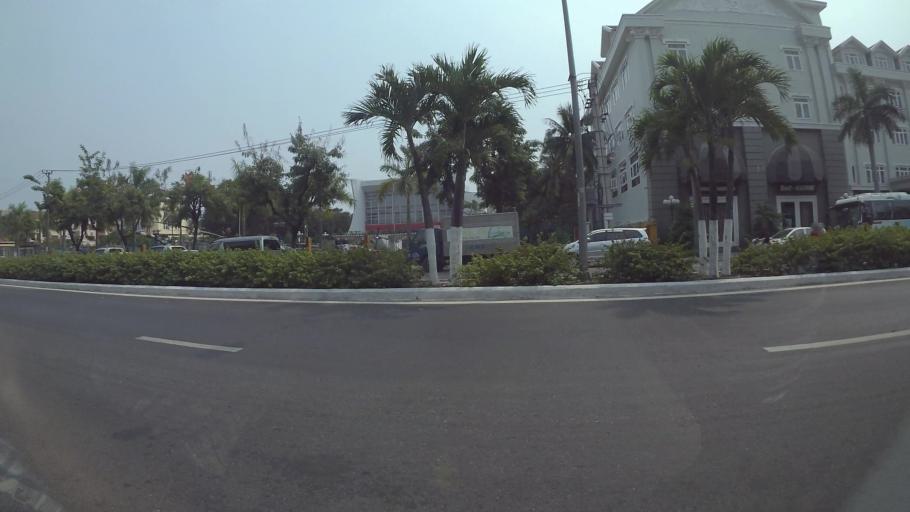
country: VN
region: Da Nang
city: Da Nang
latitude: 16.0489
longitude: 108.2169
